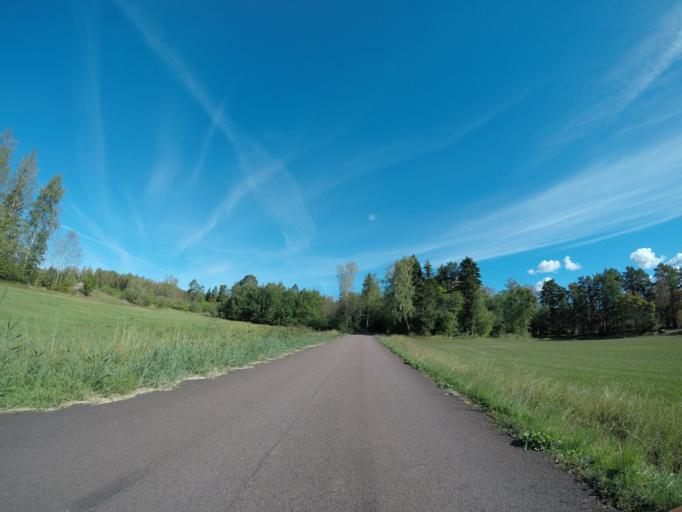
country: AX
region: Alands landsbygd
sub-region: Finstroem
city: Finstroem
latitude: 60.2977
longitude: 19.8799
